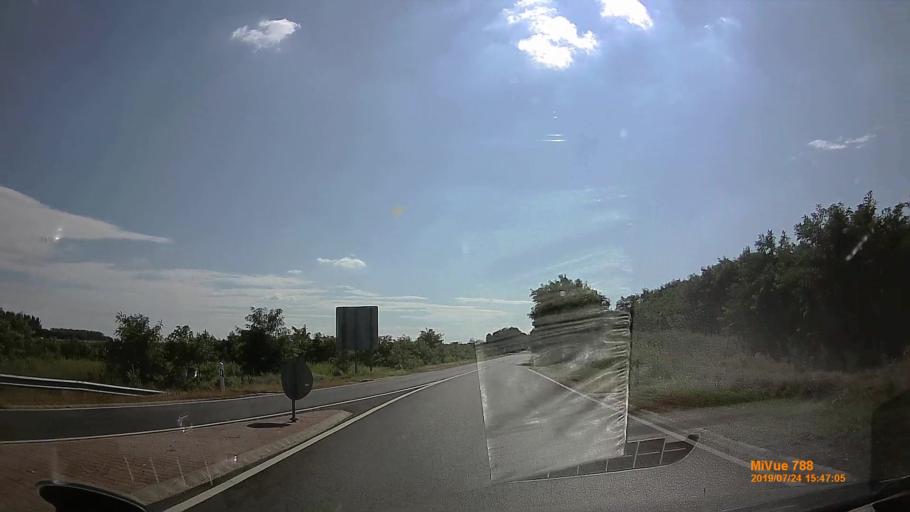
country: HU
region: Szabolcs-Szatmar-Bereg
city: Nagydobos
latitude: 48.0798
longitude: 22.2551
